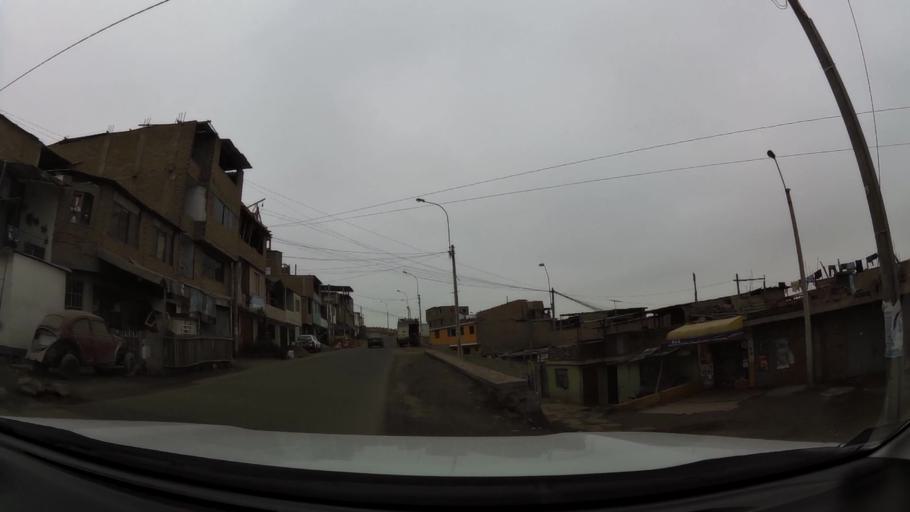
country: PE
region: Lima
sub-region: Lima
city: Surco
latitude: -12.1658
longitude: -76.9574
